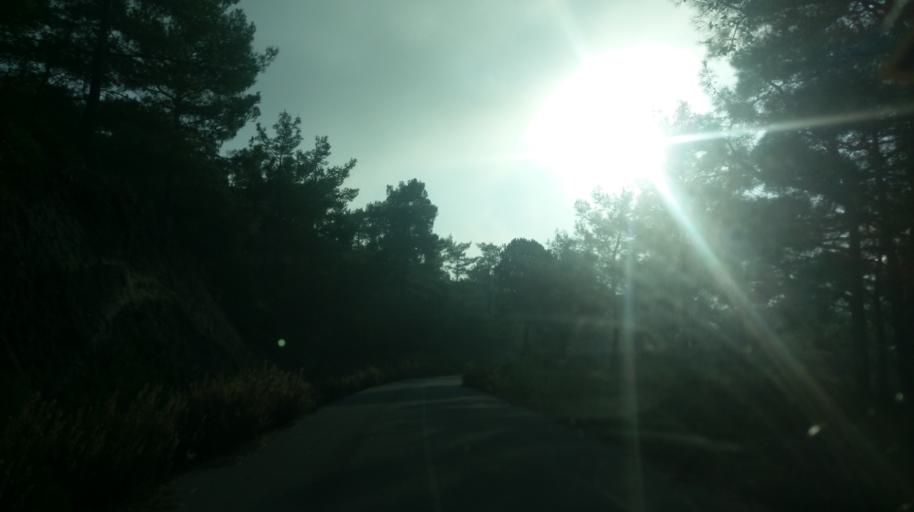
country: CY
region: Ammochostos
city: Trikomo
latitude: 35.3808
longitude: 33.8652
